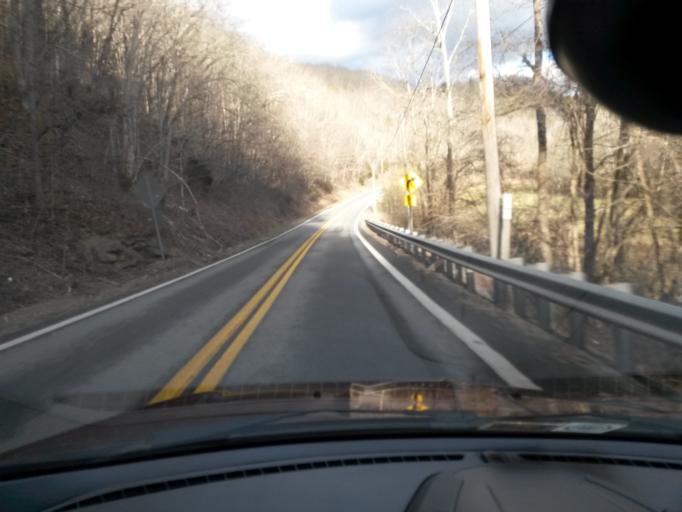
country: US
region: West Virginia
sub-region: Monroe County
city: Union
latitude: 37.5261
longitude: -80.6112
